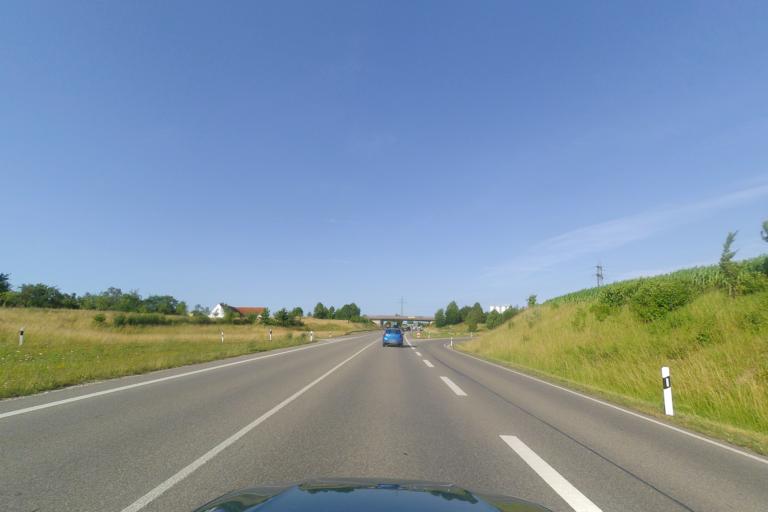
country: DE
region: Bavaria
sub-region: Swabia
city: Lauingen
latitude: 48.5761
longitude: 10.4110
